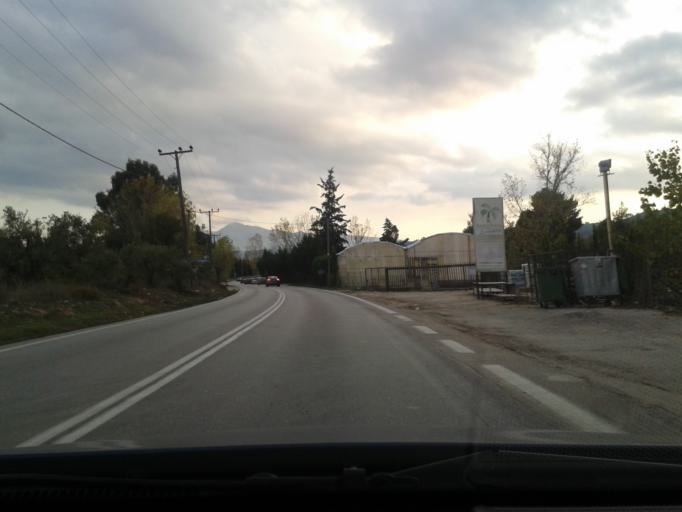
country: GR
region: Attica
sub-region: Nomarchia Anatolikis Attikis
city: Afidnes
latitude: 38.1921
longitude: 23.8539
